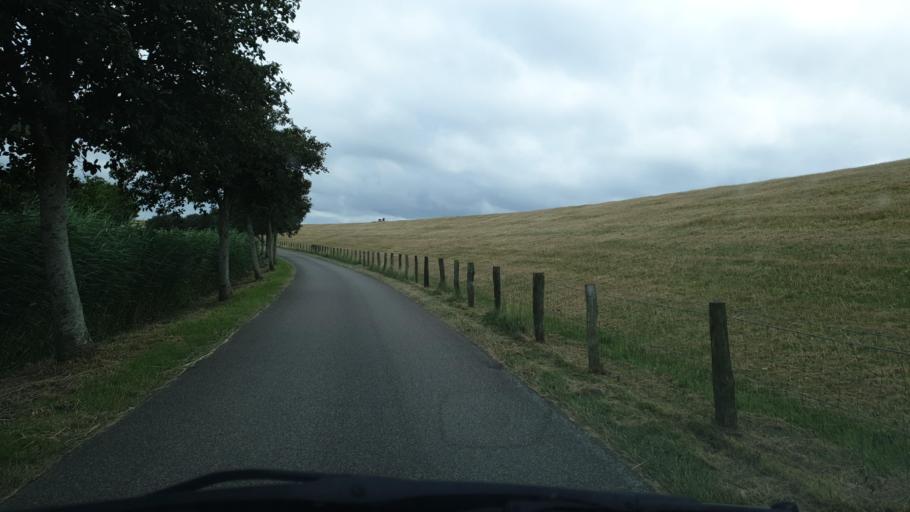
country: DE
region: Schleswig-Holstein
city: Friedrichskoog
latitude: 54.0262
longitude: 8.8388
